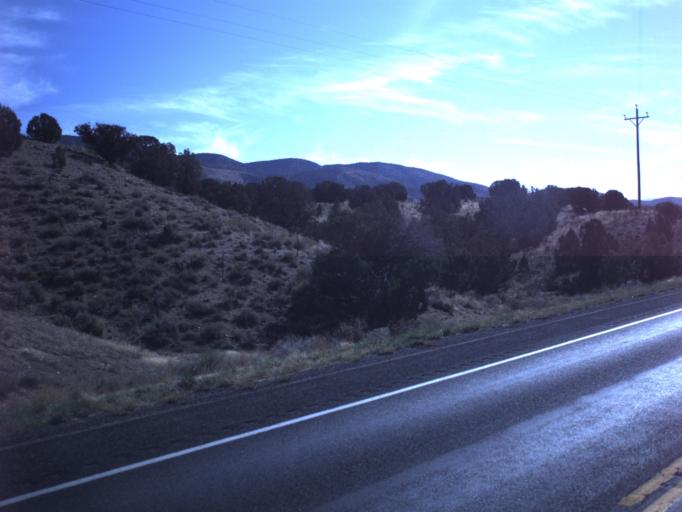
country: US
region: Utah
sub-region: Sanpete County
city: Gunnison
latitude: 39.2821
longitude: -111.8805
